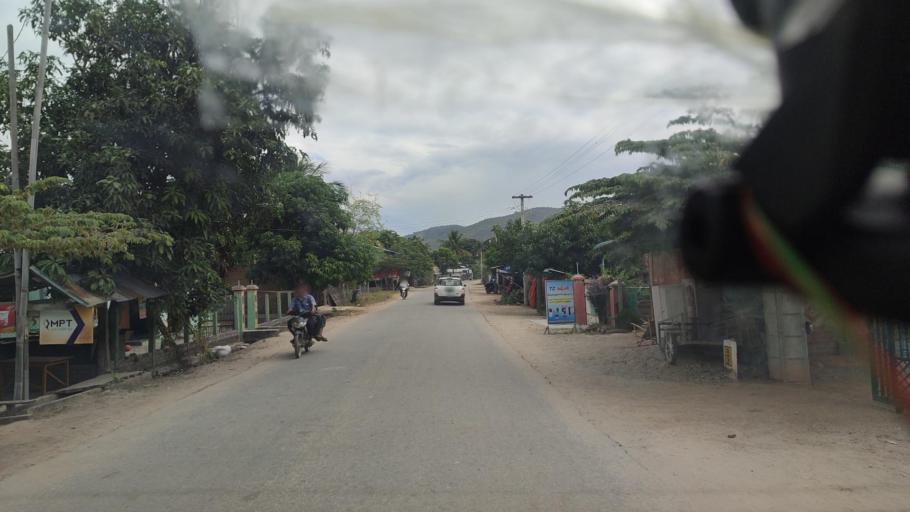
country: MM
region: Mandalay
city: Pyinmana
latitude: 19.7578
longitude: 96.3107
